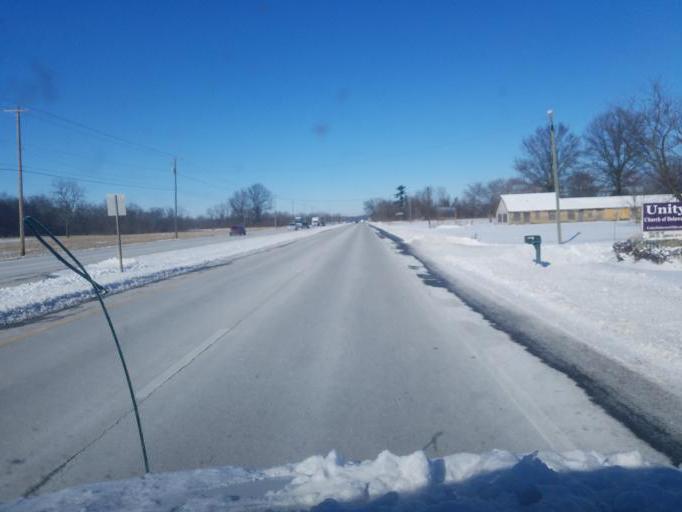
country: US
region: Ohio
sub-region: Delaware County
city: Lewis Center
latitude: 40.2355
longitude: -83.0447
